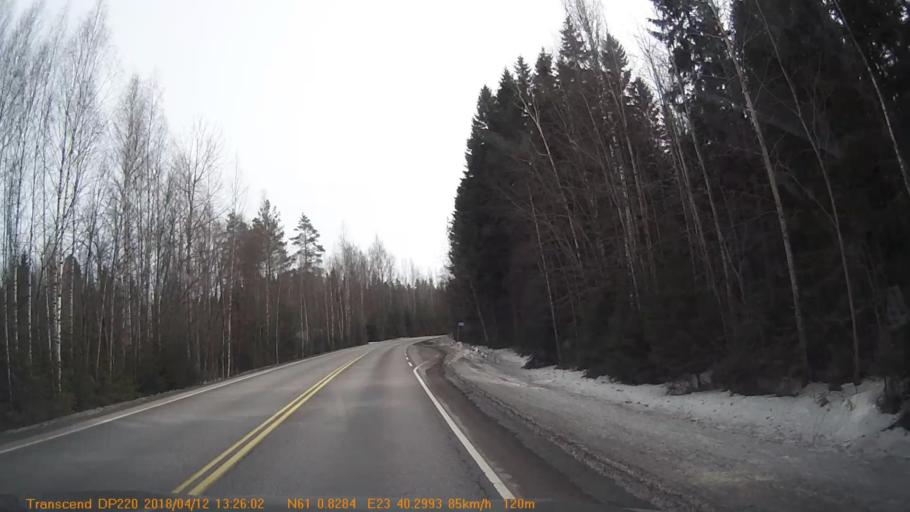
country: FI
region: Pirkanmaa
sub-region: Etelae-Pirkanmaa
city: Kylmaekoski
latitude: 61.0136
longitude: 23.6721
